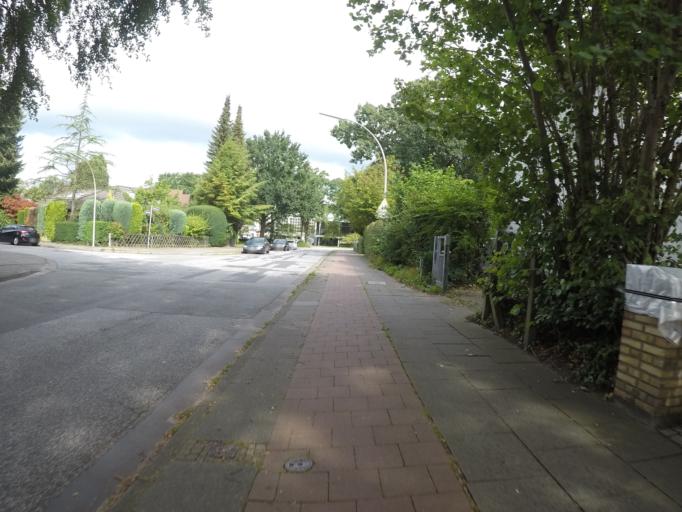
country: DE
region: Hamburg
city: Eidelstedt
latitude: 53.6137
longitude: 9.8905
